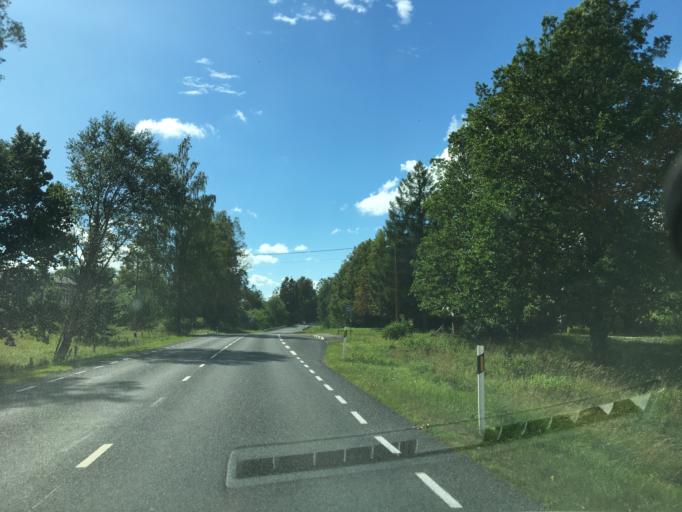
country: EE
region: Paernumaa
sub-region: Vaendra vald (alev)
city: Vandra
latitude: 58.5748
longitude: 25.2031
